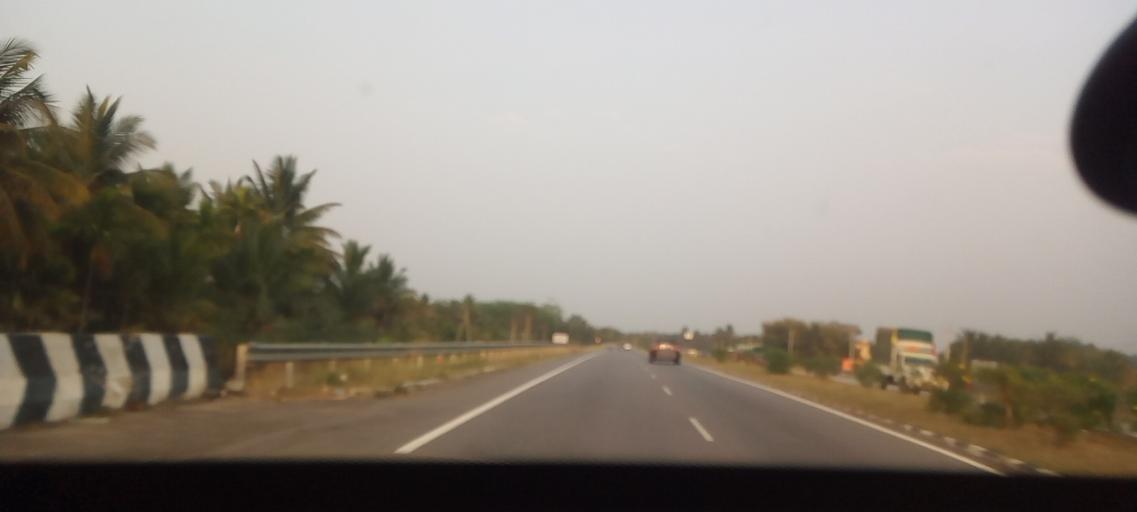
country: IN
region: Karnataka
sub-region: Tumkur
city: Kunigal
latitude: 13.0041
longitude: 76.9746
